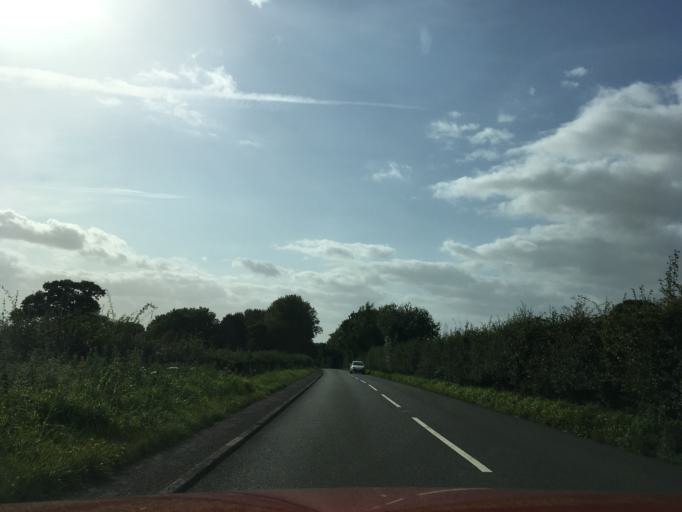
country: GB
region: England
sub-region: Gloucestershire
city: Wotton-under-Edge
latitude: 51.6351
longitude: -2.3704
